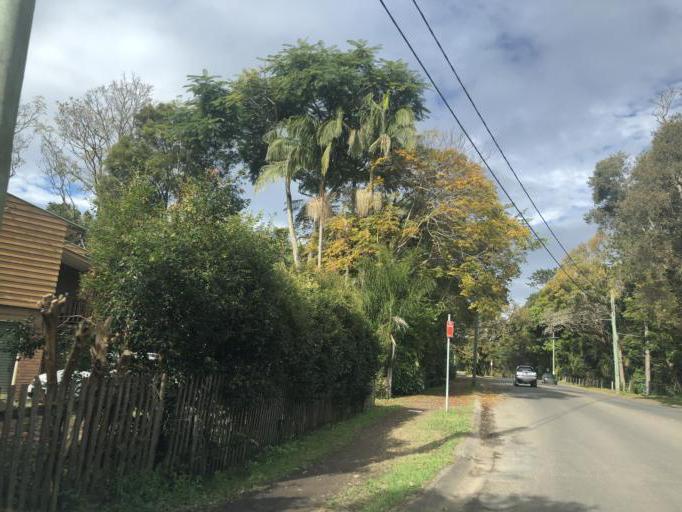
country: AU
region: New South Wales
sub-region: Bellingen
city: Bellingen
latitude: -30.4482
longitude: 152.8976
